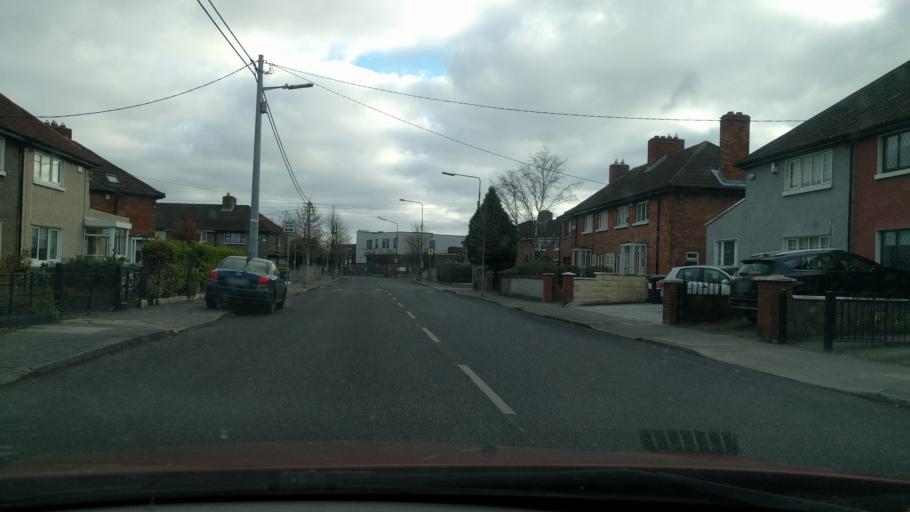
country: IE
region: Leinster
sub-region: South Dublin
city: Terenure
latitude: 53.3181
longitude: -6.2879
